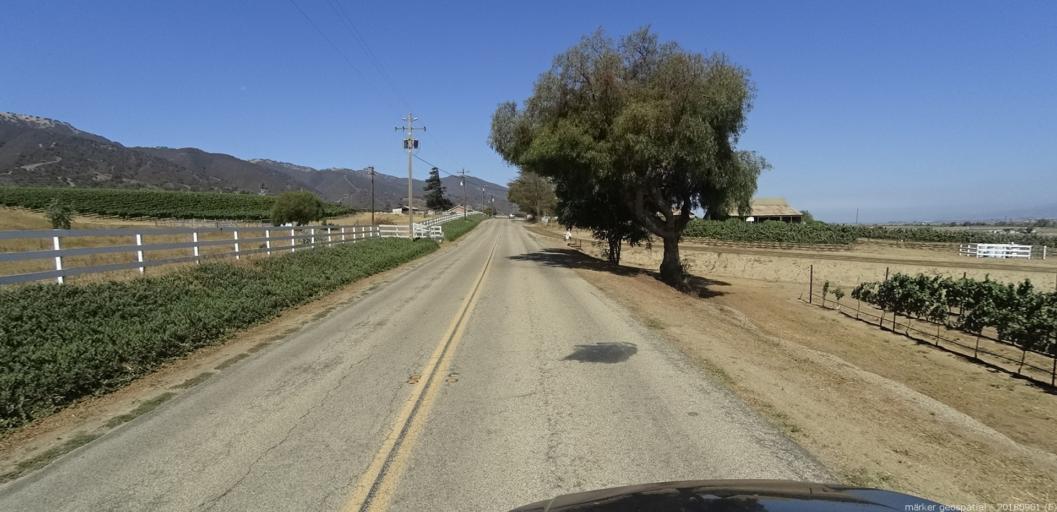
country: US
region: California
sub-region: Monterey County
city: Gonzales
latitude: 36.5044
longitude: -121.5080
